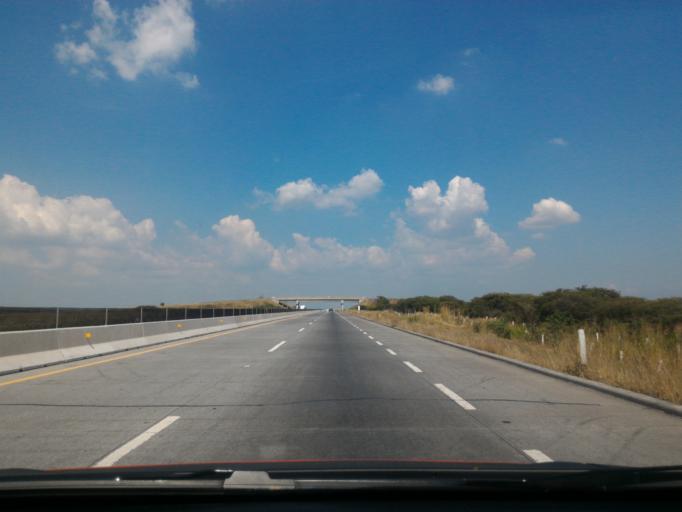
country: MX
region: Jalisco
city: Degollado
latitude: 20.3850
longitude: -102.1152
